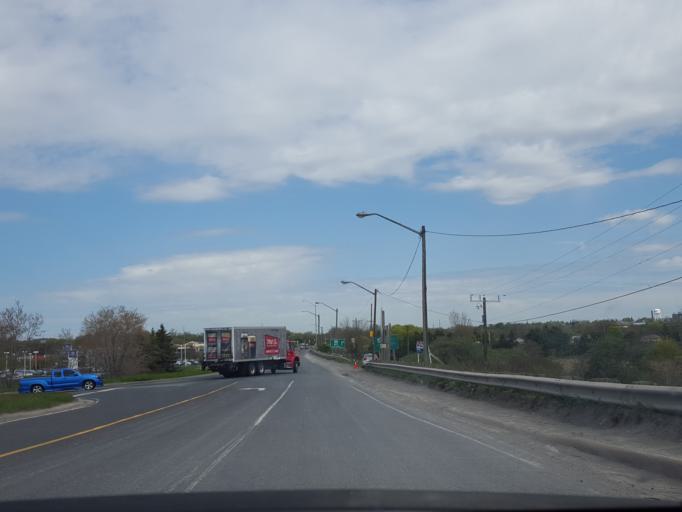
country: CA
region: Ontario
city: Oshawa
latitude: 43.8926
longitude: -78.6885
